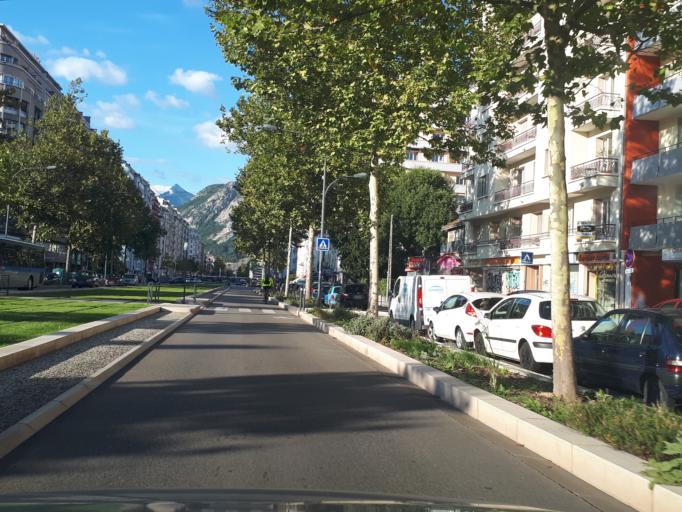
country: FR
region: Rhone-Alpes
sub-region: Departement de l'Isere
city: Grenoble
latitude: 45.1763
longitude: 5.7153
